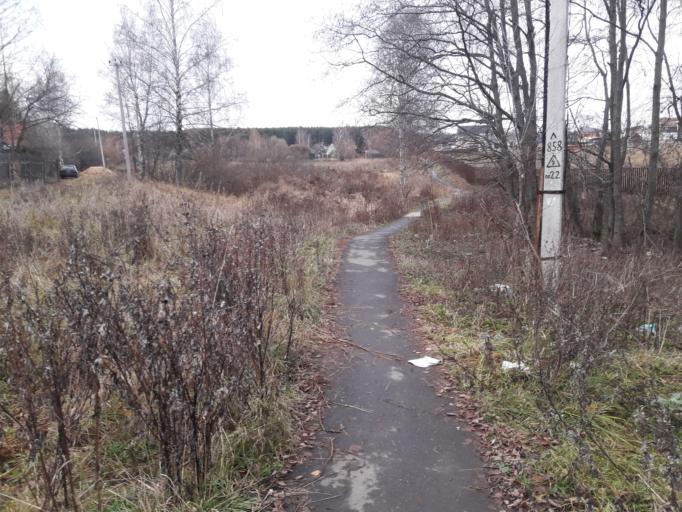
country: RU
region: Moskovskaya
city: Ashukino
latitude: 56.1668
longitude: 37.9347
